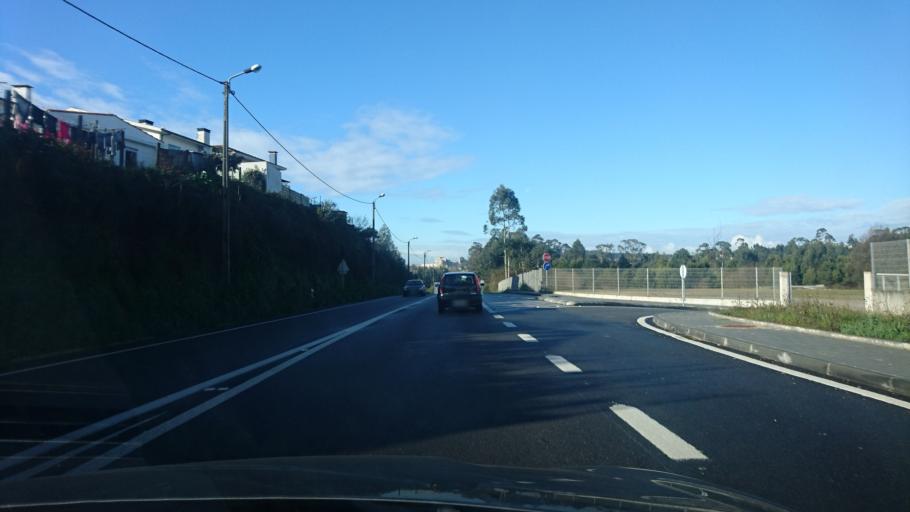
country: PT
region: Aveiro
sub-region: Santa Maria da Feira
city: Feira
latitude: 40.9311
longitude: -8.5286
